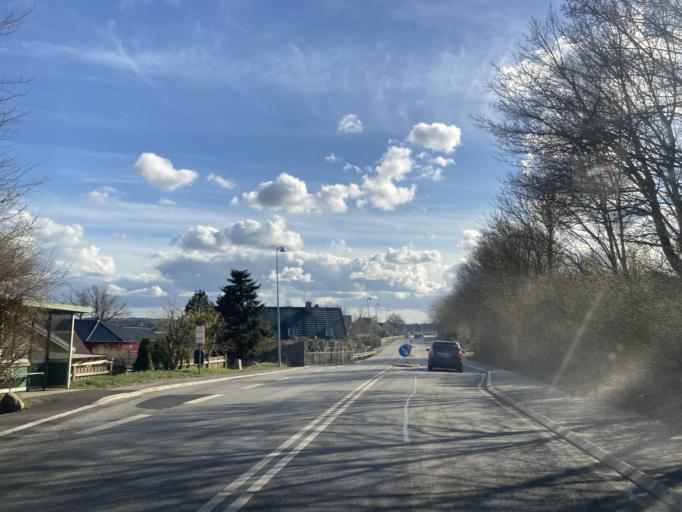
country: DK
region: Zealand
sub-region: Lejre Kommune
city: Lejre
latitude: 55.6700
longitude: 11.9309
